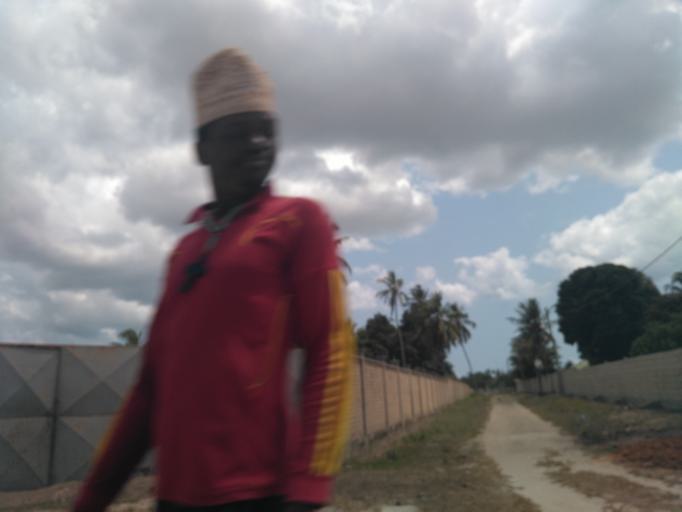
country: TZ
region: Dar es Salaam
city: Dar es Salaam
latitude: -6.8779
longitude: 39.3440
